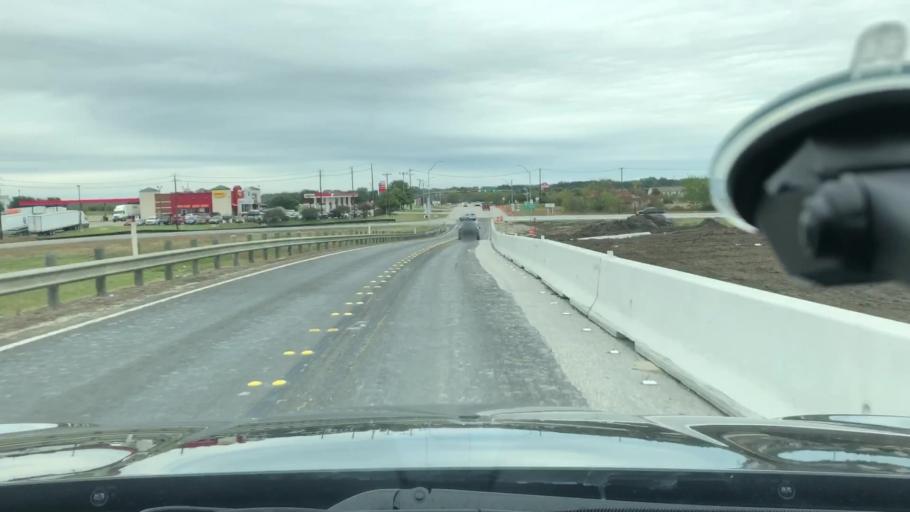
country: US
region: Texas
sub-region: Kaufman County
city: Terrell
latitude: 32.7212
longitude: -96.3193
